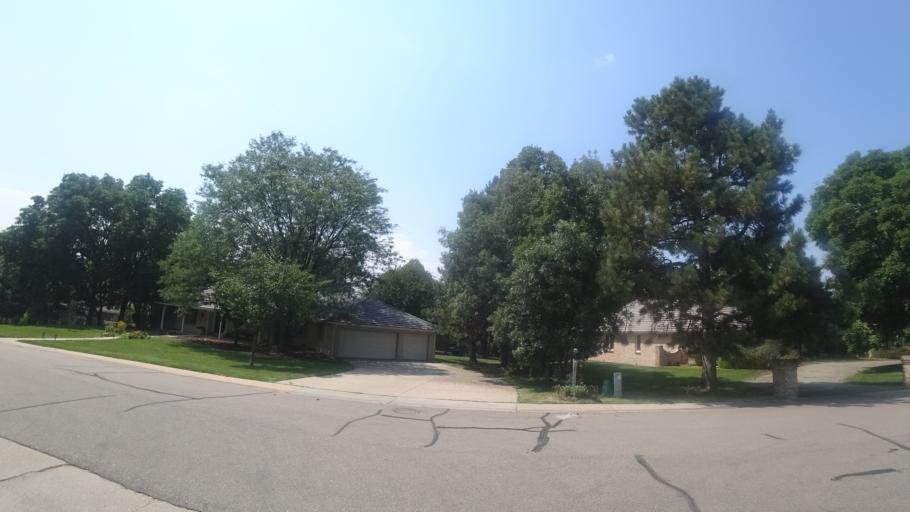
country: US
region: Colorado
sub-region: Arapahoe County
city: Greenwood Village
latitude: 39.6136
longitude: -104.9746
